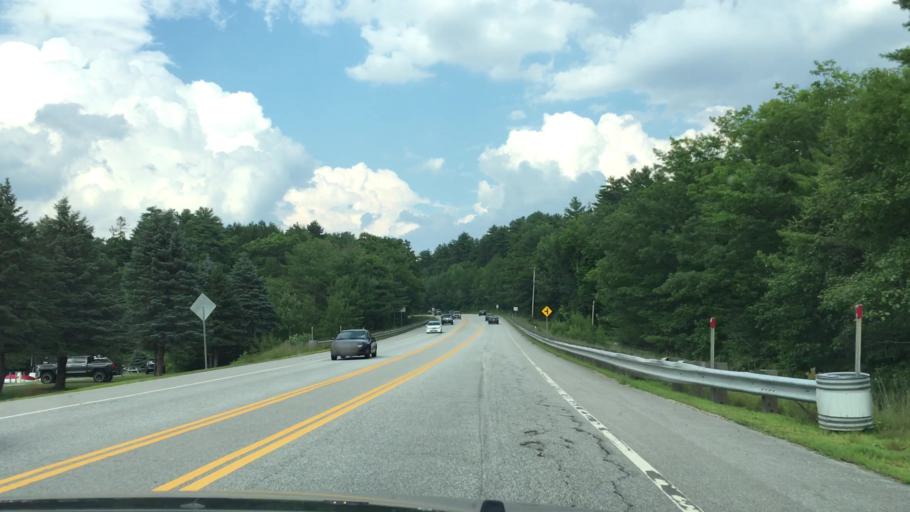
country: US
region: New Hampshire
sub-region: Belknap County
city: Gilford
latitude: 43.5798
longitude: -71.3935
